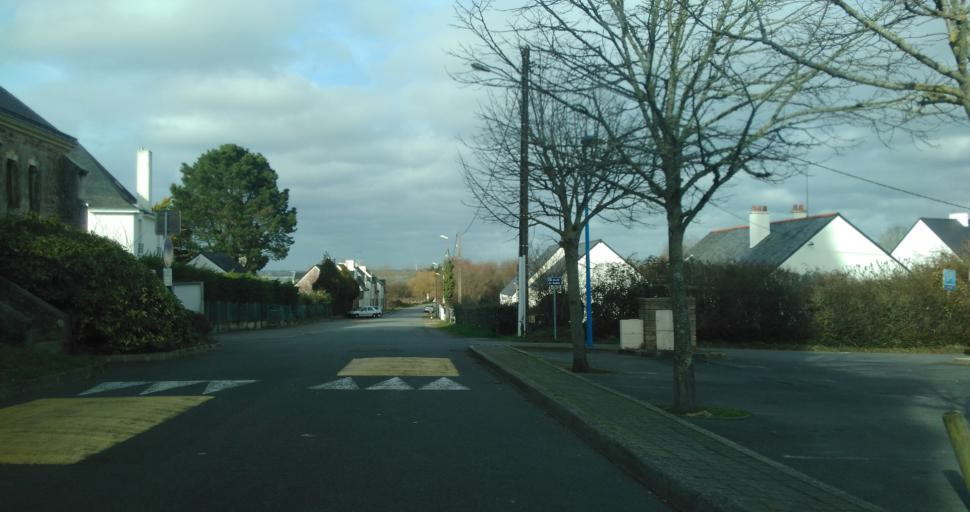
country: FR
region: Brittany
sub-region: Departement du Morbihan
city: Penestin
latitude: 47.4838
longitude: -2.4726
